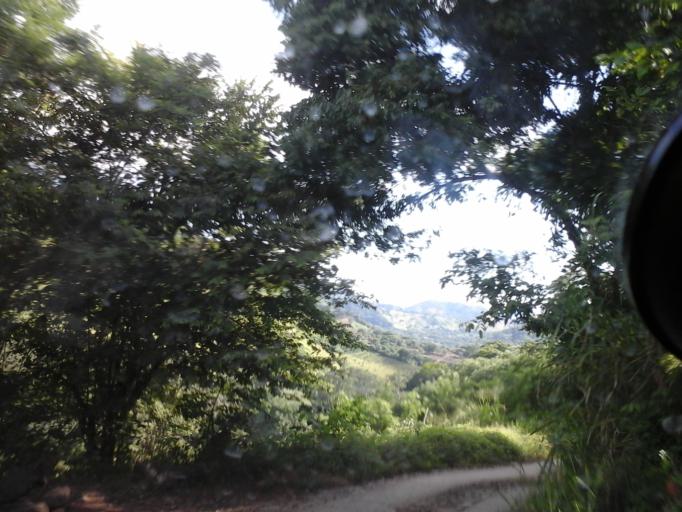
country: CO
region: Cesar
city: San Diego
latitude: 10.2671
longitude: -73.1007
